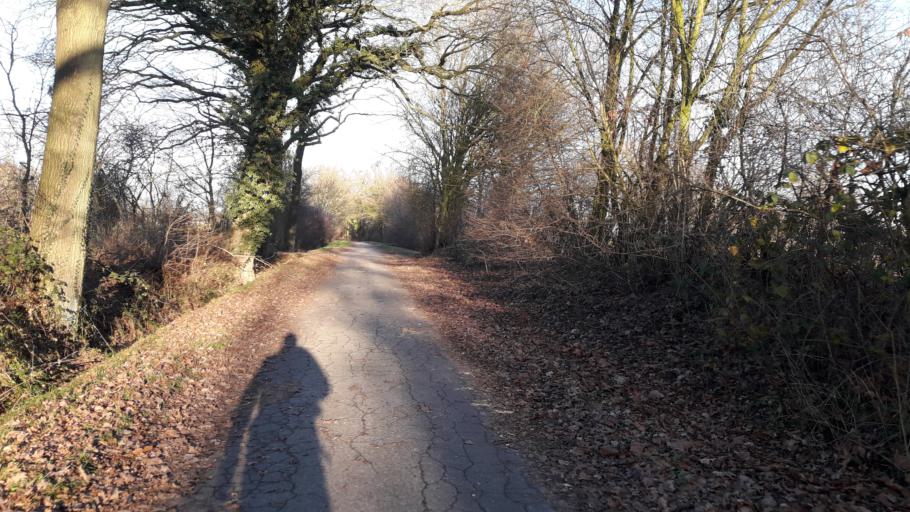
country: DE
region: Schleswig-Holstein
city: Quickborn
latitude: 53.7174
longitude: 9.8621
